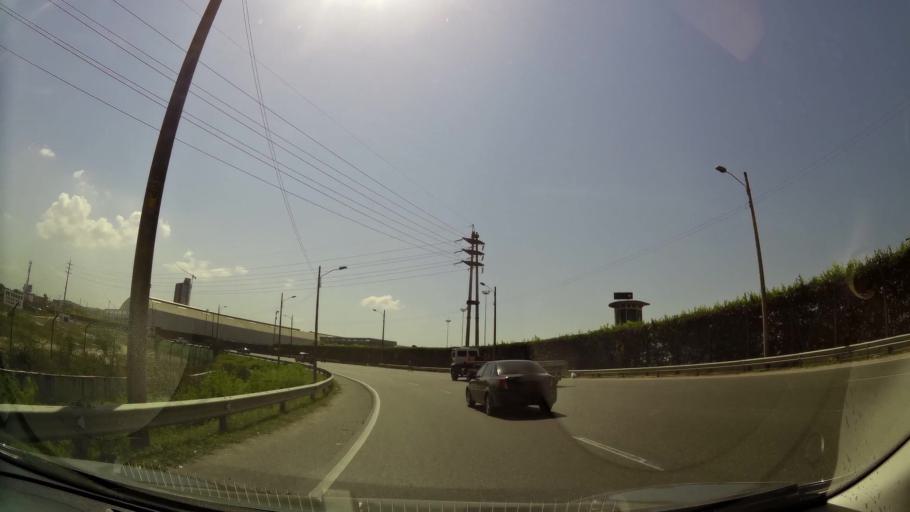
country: CO
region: Bolivar
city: Cartagena
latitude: 10.3811
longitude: -75.5058
